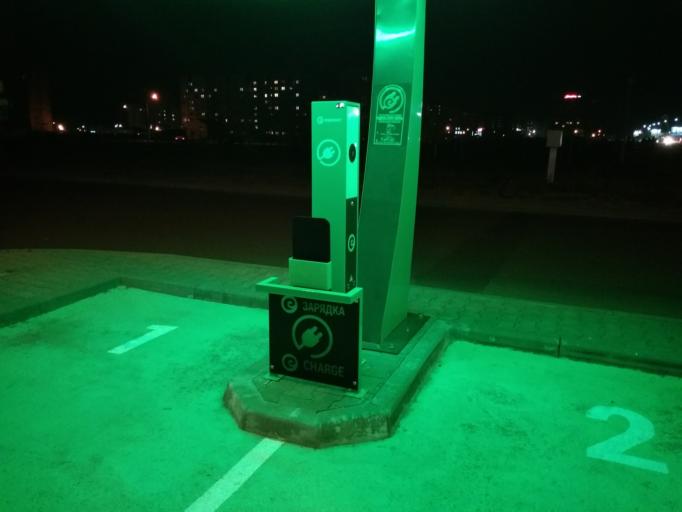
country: BY
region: Brest
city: Brest
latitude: 52.0761
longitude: 23.7167
